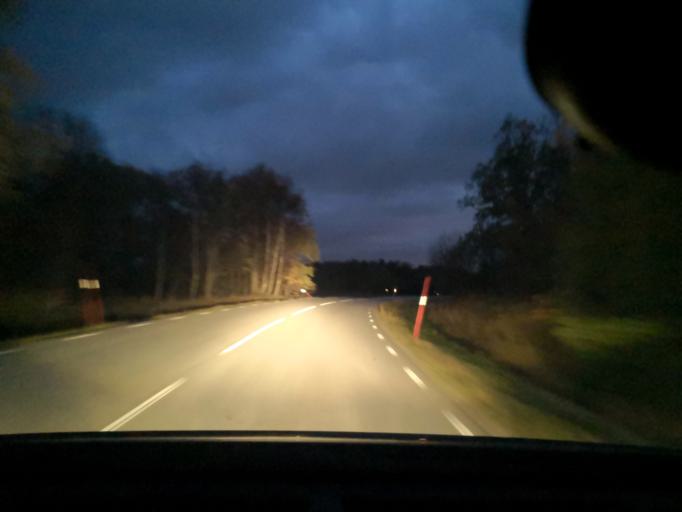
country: SE
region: Uppsala
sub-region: Enkopings Kommun
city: Hummelsta
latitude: 59.5487
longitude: 16.8667
